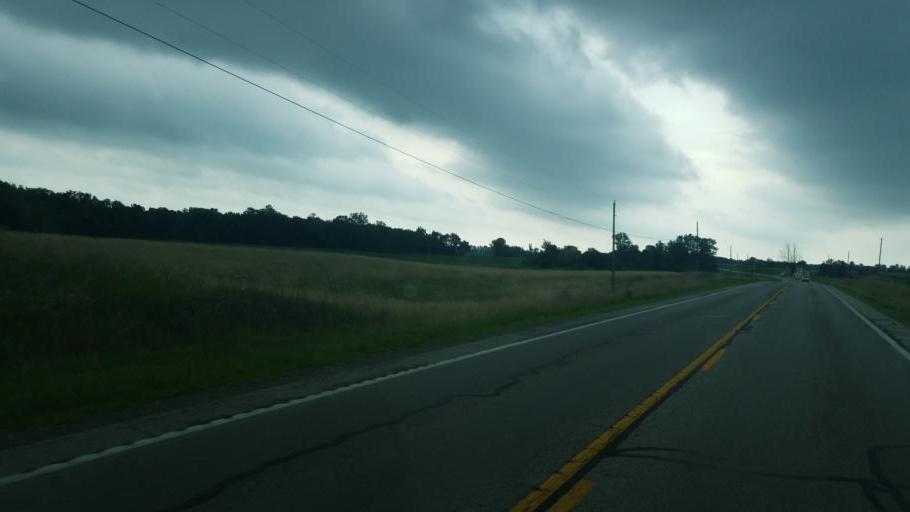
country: US
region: Ohio
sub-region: Logan County
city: Russells Point
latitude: 40.5518
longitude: -83.8370
